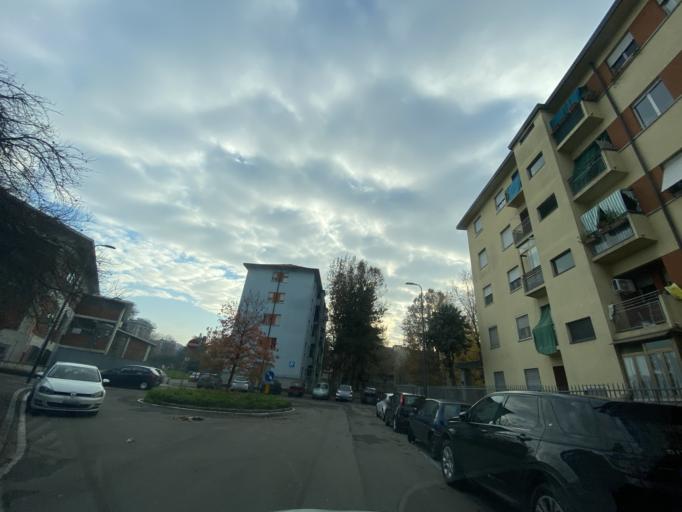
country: IT
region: Lombardy
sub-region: Citta metropolitana di Milano
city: Bresso
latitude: 45.5126
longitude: 9.1951
